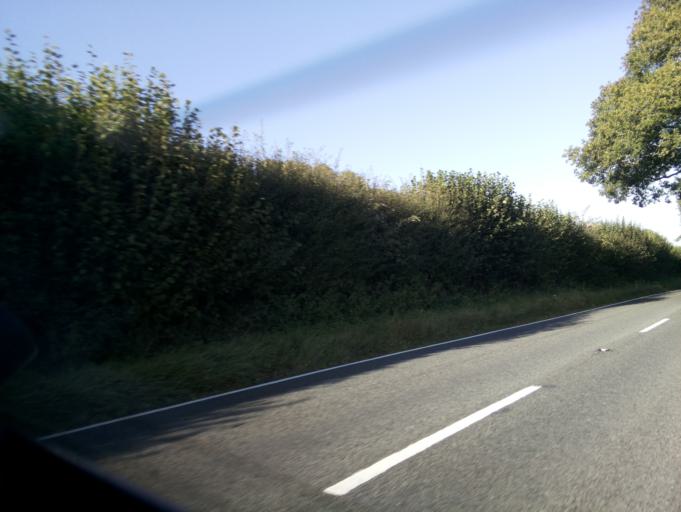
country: GB
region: England
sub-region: Hampshire
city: Swanmore
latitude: 50.9308
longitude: -1.1477
